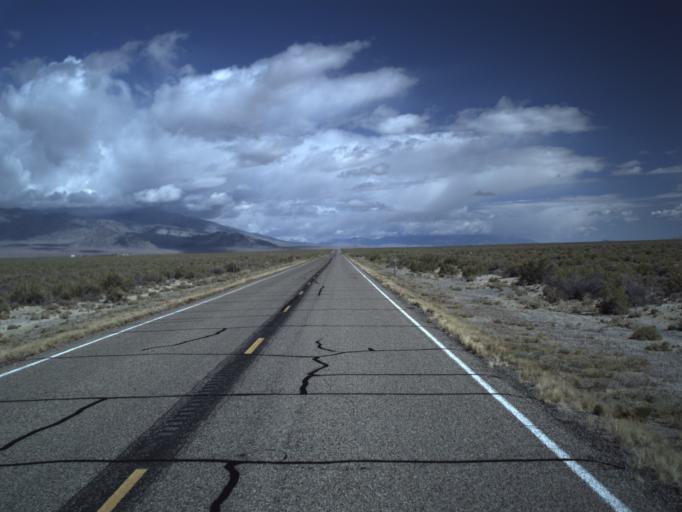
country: US
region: Nevada
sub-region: White Pine County
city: McGill
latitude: 39.0165
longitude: -114.0353
